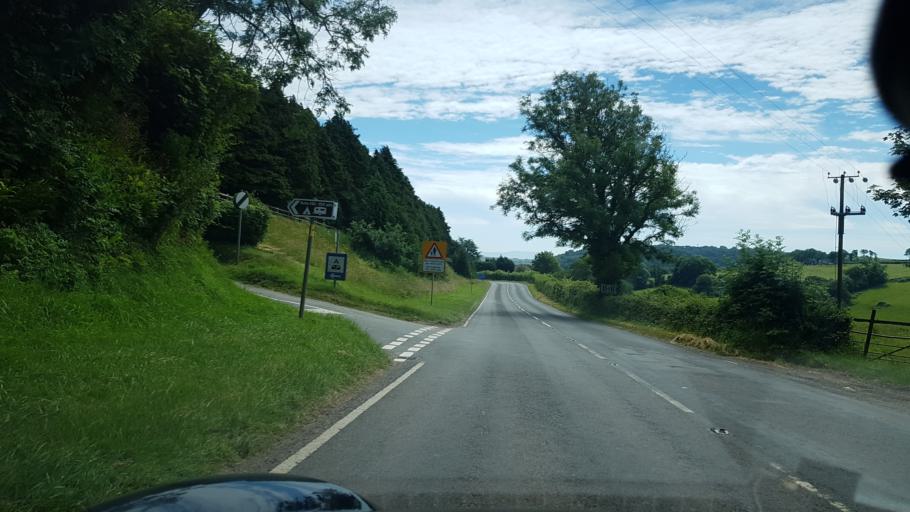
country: GB
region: Wales
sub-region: Carmarthenshire
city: Saint Clears
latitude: 51.7791
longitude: -4.4697
